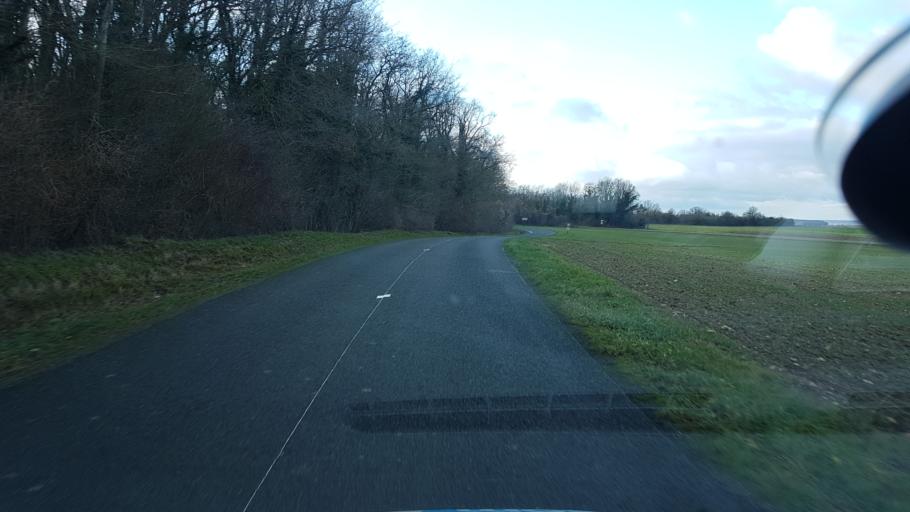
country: FR
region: Ile-de-France
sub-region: Departement de Seine-et-Marne
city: Montigny-sur-Loing
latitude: 48.2762
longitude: 2.7621
